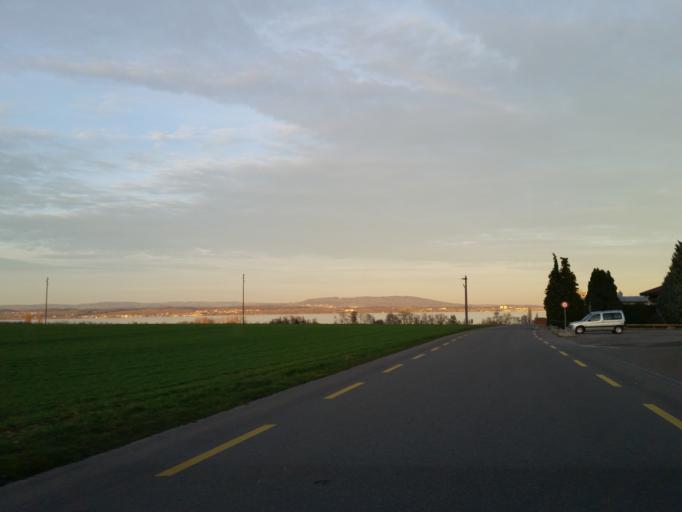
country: CH
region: Thurgau
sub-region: Kreuzlingen District
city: Guttingen
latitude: 47.6064
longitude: 9.2834
